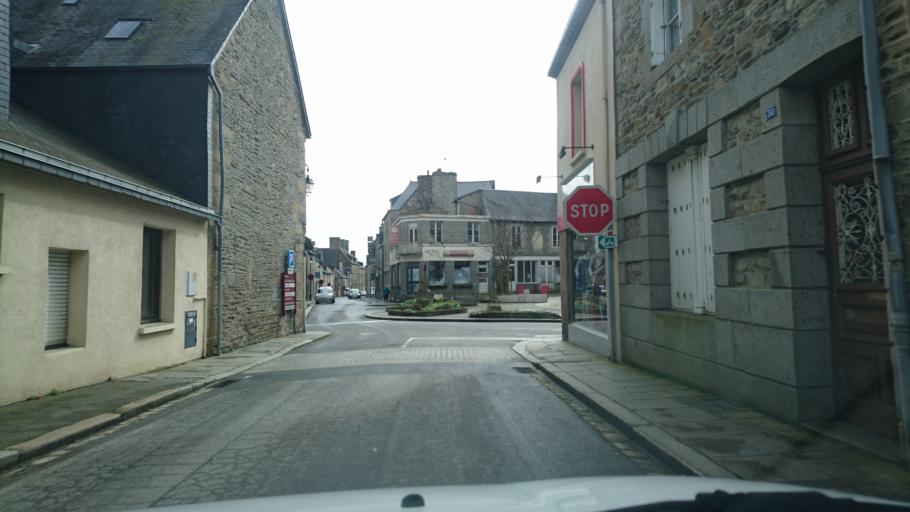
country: FR
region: Brittany
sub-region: Departement d'Ille-et-Vilaine
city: Antrain
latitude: 48.4611
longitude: -1.4851
